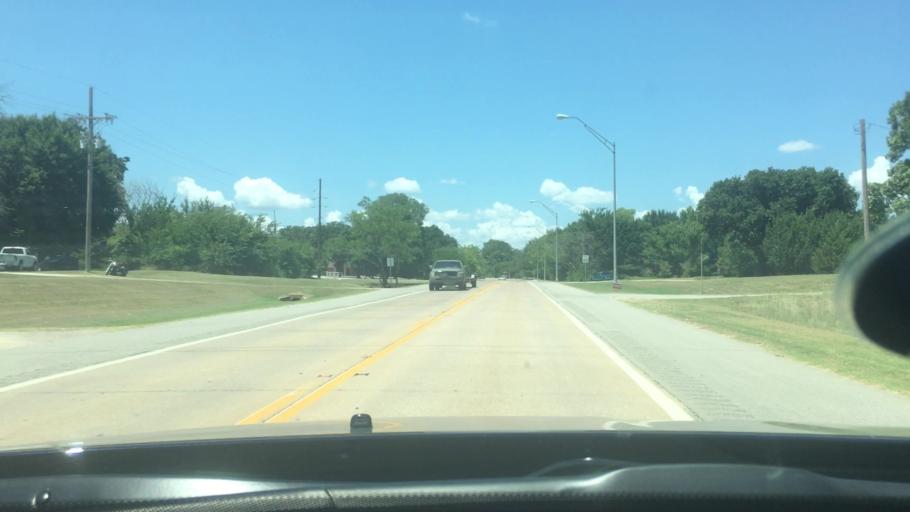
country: US
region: Oklahoma
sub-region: Bryan County
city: Durant
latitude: 34.0149
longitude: -96.1264
